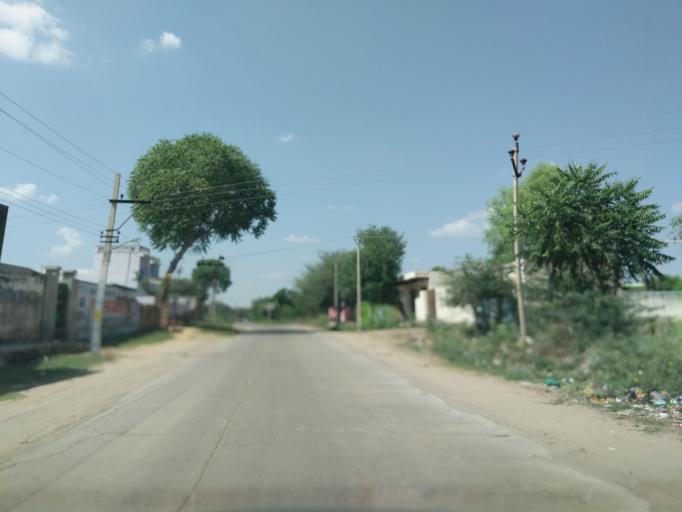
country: IN
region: Rajasthan
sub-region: Jhunjhunun
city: Jhunjhunun
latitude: 28.1390
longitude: 75.3896
